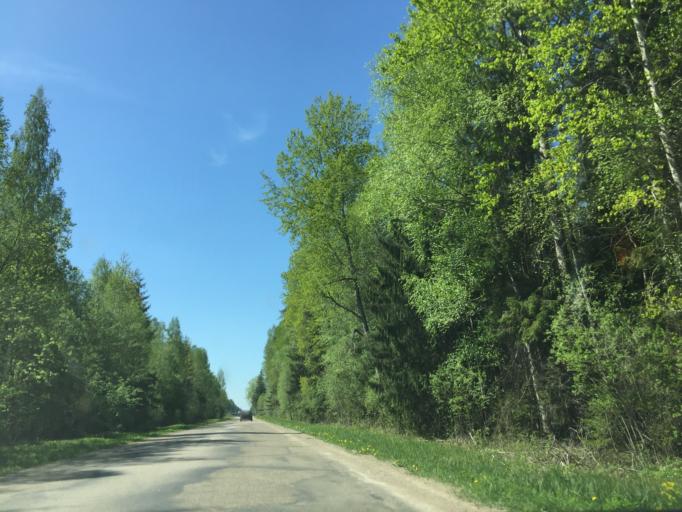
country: LV
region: Ogre
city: Ogre
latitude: 56.8506
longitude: 24.6865
